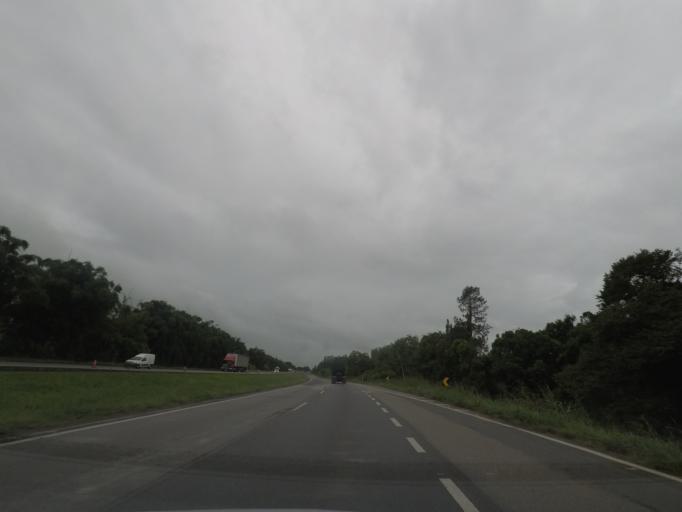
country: BR
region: Sao Paulo
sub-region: Jacupiranga
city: Jacupiranga
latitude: -24.7222
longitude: -48.0436
